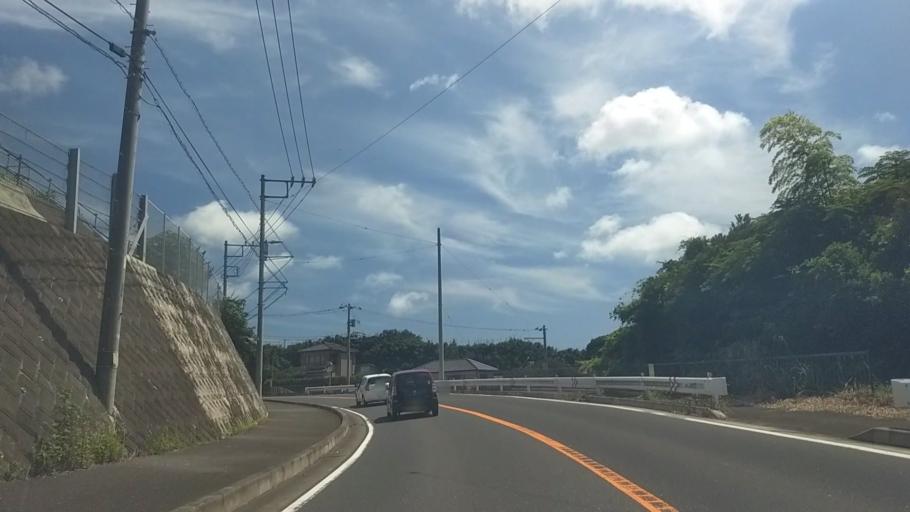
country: JP
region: Kanagawa
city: Miura
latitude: 35.2015
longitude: 139.6500
